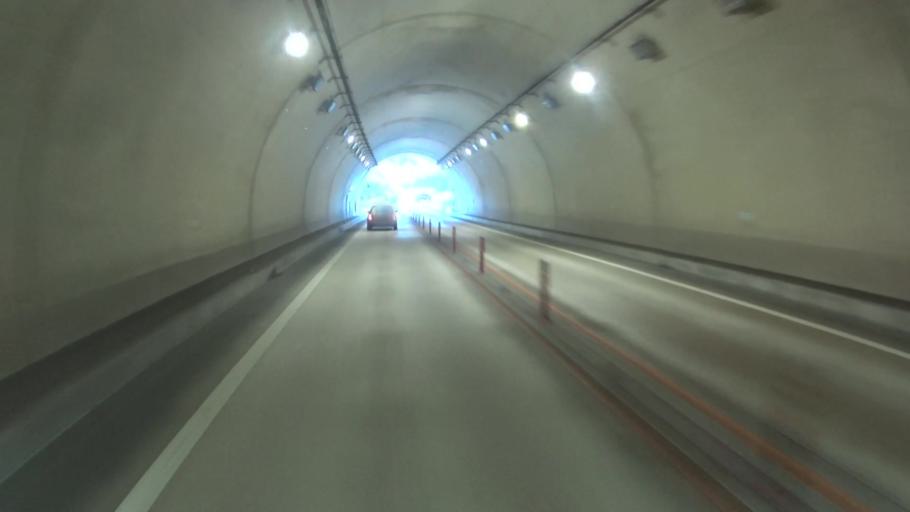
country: JP
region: Kyoto
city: Miyazu
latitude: 35.5440
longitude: 135.1542
